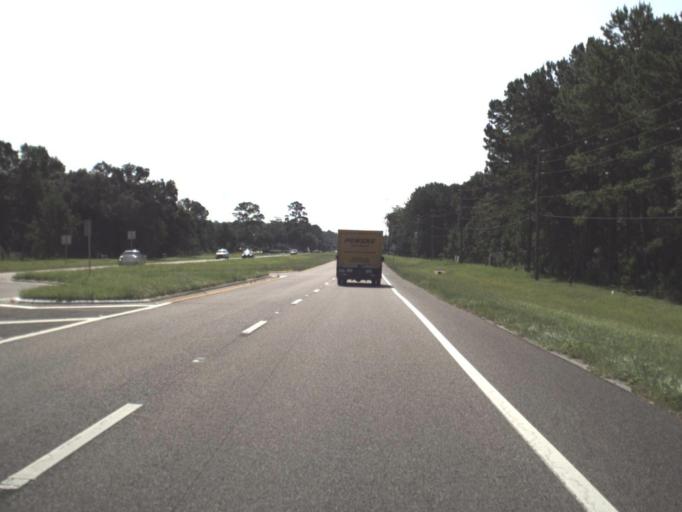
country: US
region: Florida
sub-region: Hernando County
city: South Brooksville
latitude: 28.5435
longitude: -82.4159
